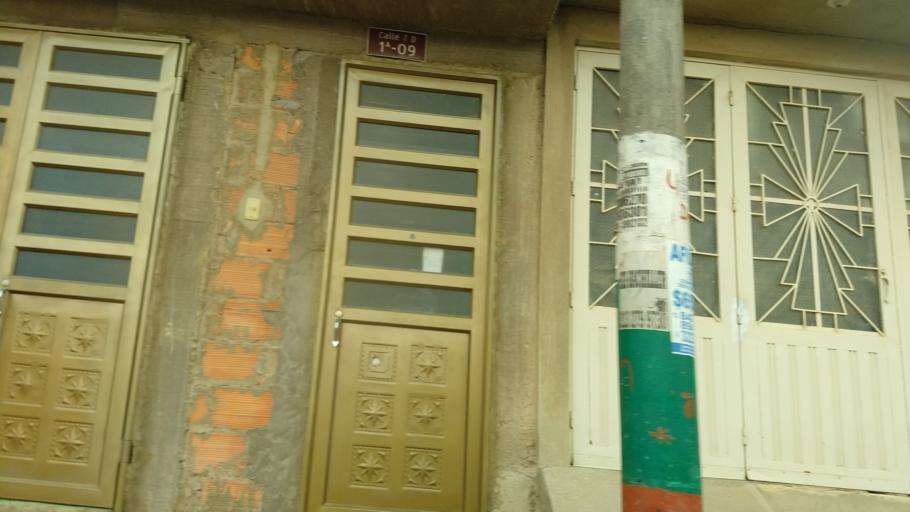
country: CO
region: Cundinamarca
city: Soacha
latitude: 4.5734
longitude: -74.2195
